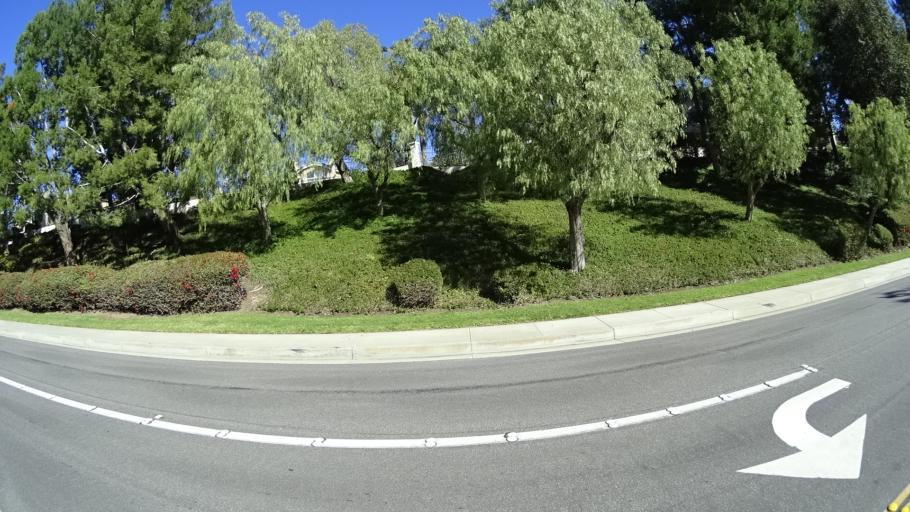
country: US
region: California
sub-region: Orange County
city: Yorba Linda
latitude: 33.8580
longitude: -117.7454
